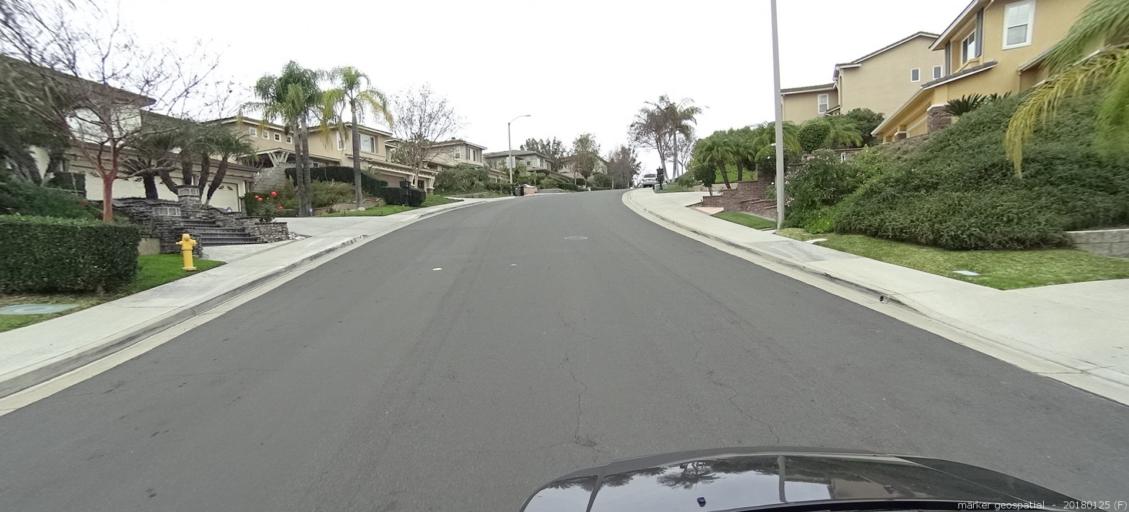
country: US
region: California
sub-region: Los Angeles County
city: Walnut
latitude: 33.9707
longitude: -117.8540
